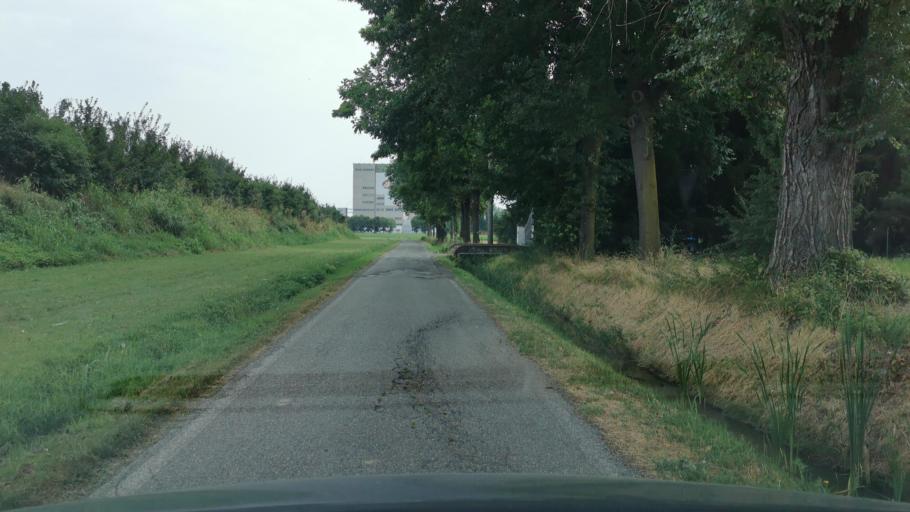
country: IT
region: Emilia-Romagna
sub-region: Provincia di Modena
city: Villanova
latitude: 44.6990
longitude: 10.9066
